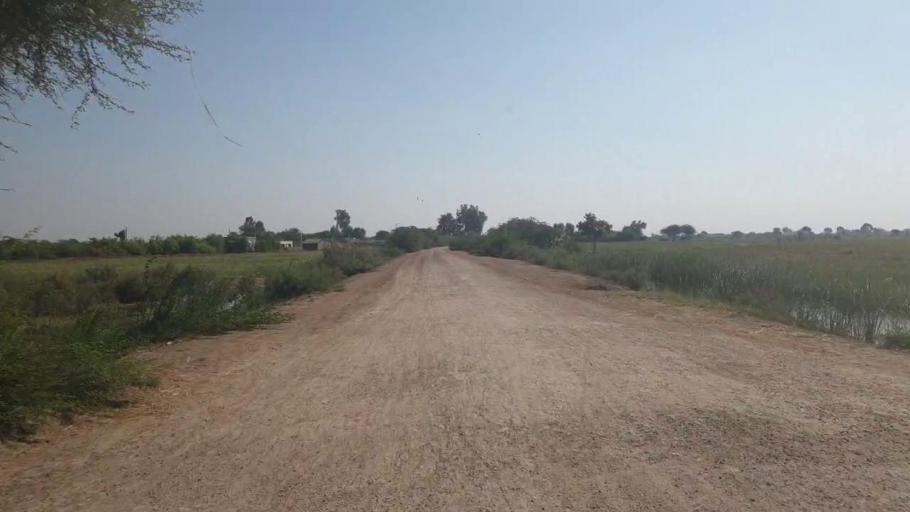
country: PK
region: Sindh
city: Badin
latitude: 24.5727
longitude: 68.8444
